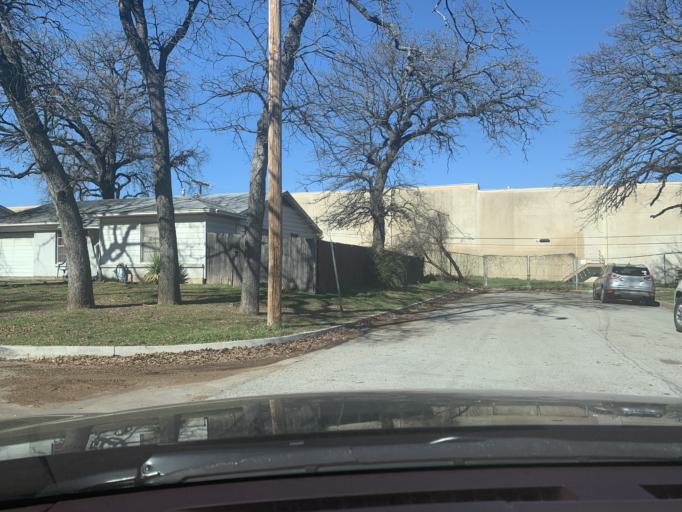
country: US
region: Texas
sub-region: Tarrant County
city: Haltom City
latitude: 32.7703
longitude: -97.2824
